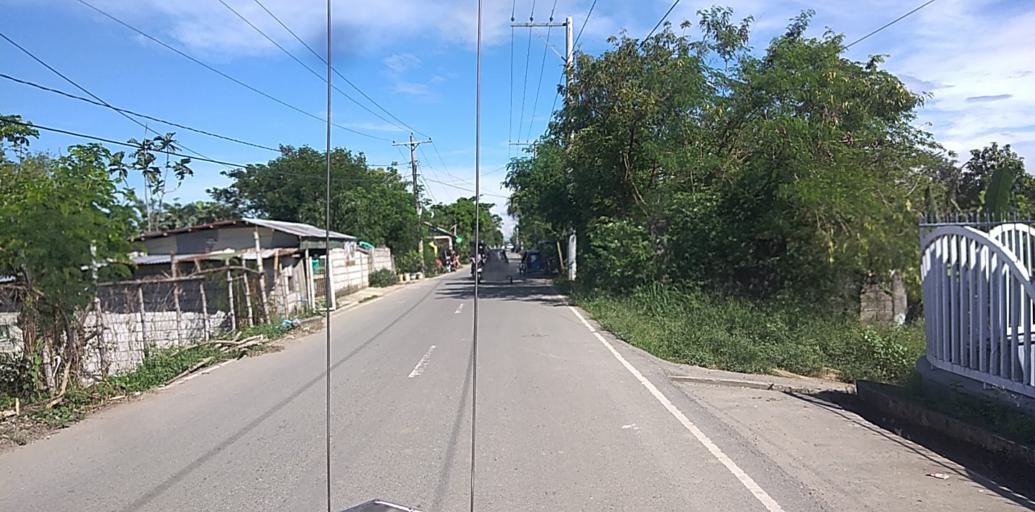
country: PH
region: Central Luzon
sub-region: Province of Pampanga
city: Candaba
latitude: 15.0860
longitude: 120.8103
